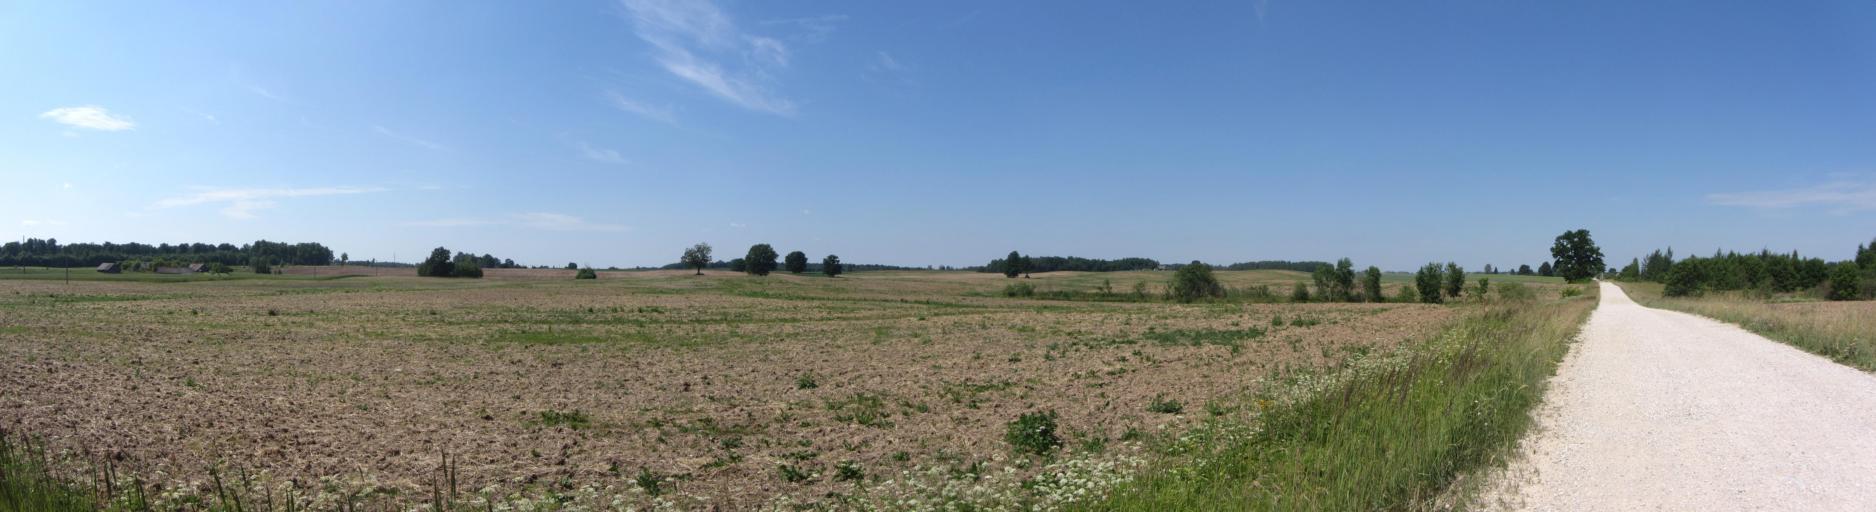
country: LT
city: Sirvintos
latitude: 55.2203
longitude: 24.9419
